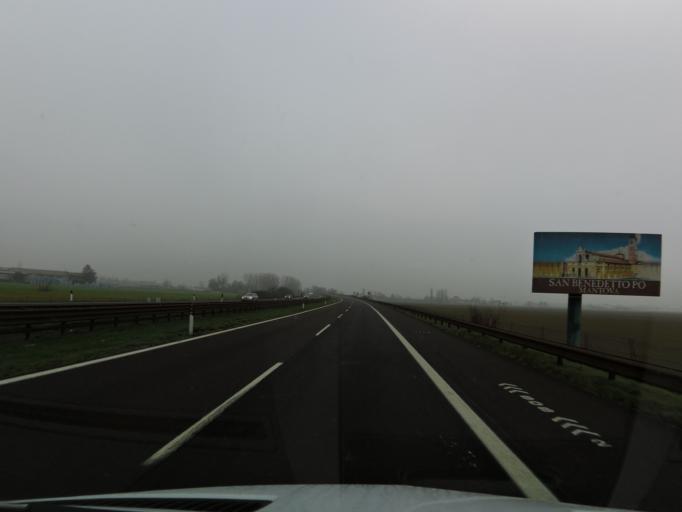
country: IT
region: Lombardy
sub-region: Provincia di Mantova
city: Bondeno
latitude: 44.9361
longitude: 10.8630
